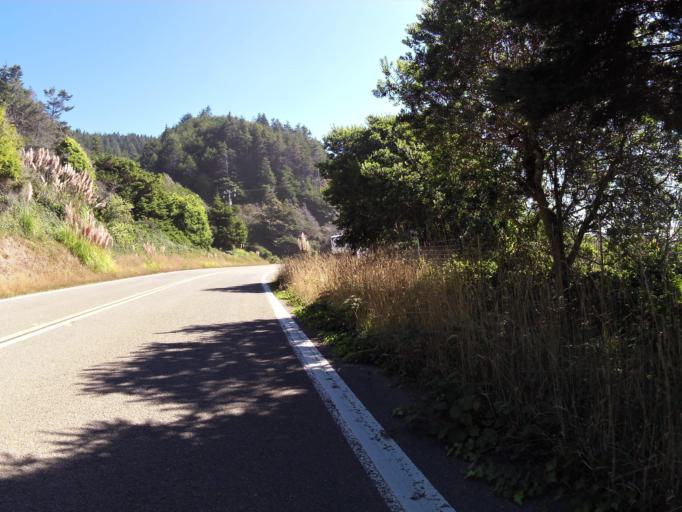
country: US
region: California
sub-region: Mendocino County
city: Fort Bragg
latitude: 39.6990
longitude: -123.8011
